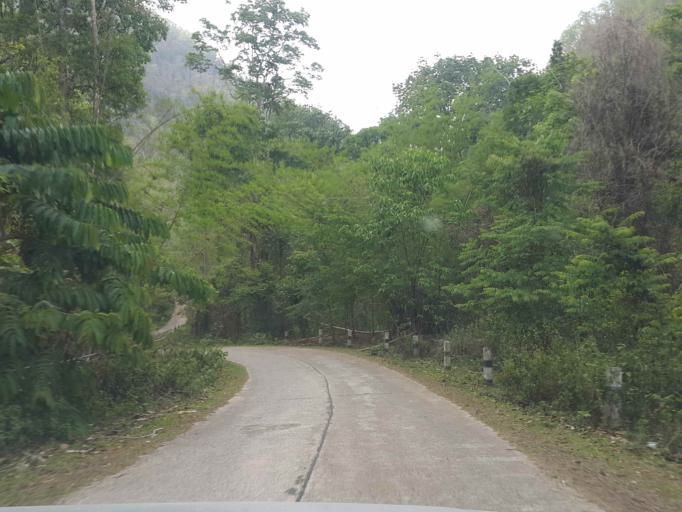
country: TH
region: Chiang Mai
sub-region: Amphoe Chiang Dao
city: Chiang Dao
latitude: 19.3876
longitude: 98.7696
